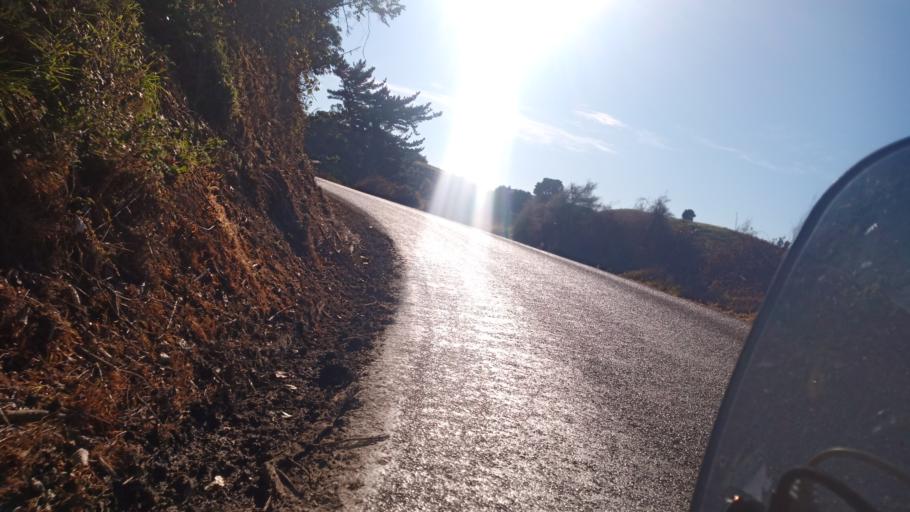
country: NZ
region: Hawke's Bay
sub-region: Wairoa District
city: Wairoa
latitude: -38.8603
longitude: 177.2390
